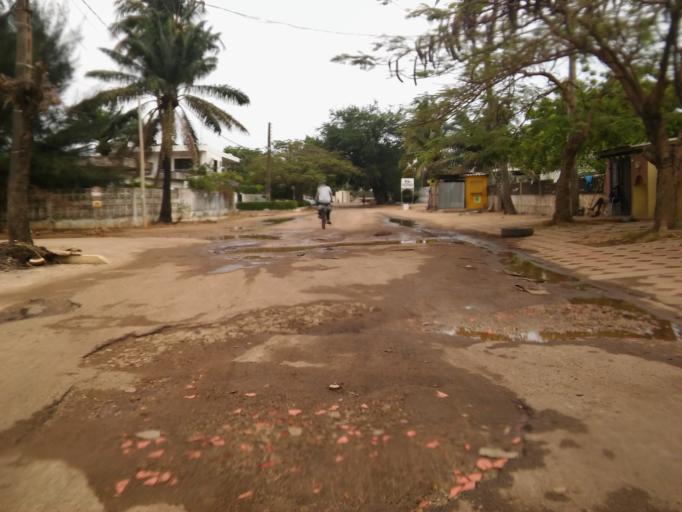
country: BJ
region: Littoral
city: Cotonou
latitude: 6.3549
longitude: 2.3961
